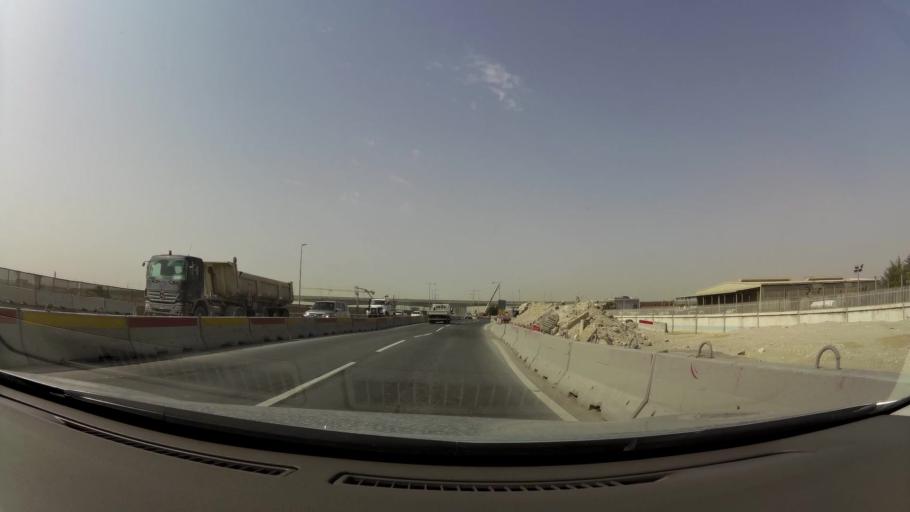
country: QA
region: Baladiyat ad Dawhah
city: Doha
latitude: 25.2291
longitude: 51.5127
